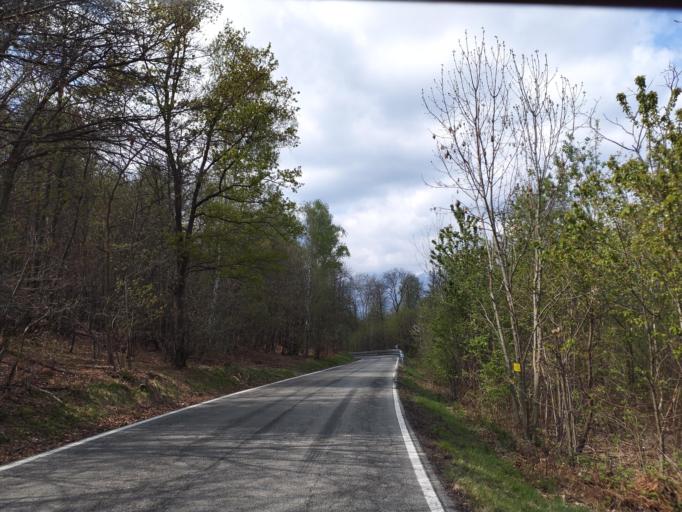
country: IT
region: Piedmont
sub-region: Provincia di Torino
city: Palazzo Canavese
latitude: 45.4778
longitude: 7.9780
